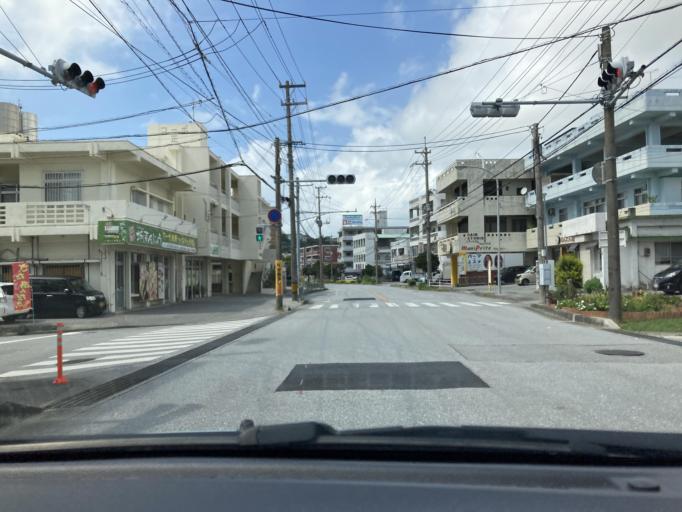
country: JP
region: Okinawa
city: Chatan
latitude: 26.3011
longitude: 127.7997
